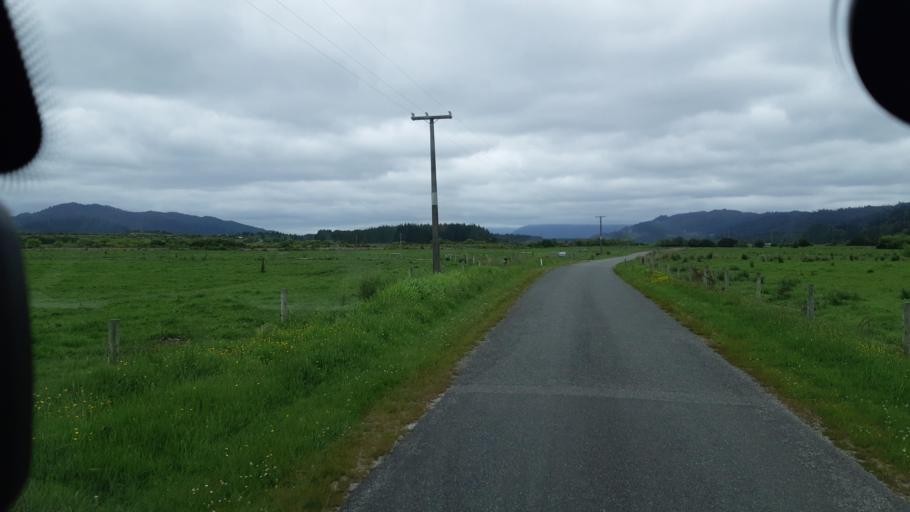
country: NZ
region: West Coast
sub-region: Westland District
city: Hokitika
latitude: -42.7100
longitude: 171.0673
